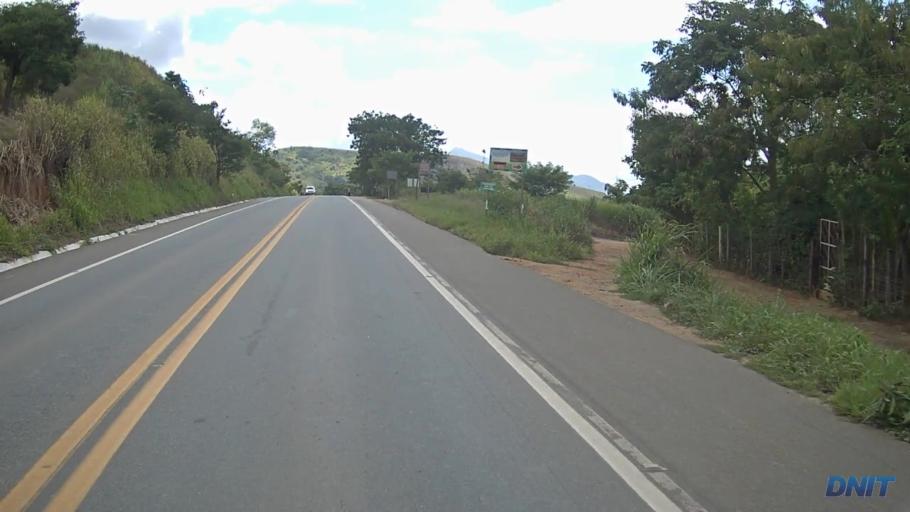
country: BR
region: Minas Gerais
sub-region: Governador Valadares
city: Governador Valadares
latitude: -18.9279
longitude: -42.0411
